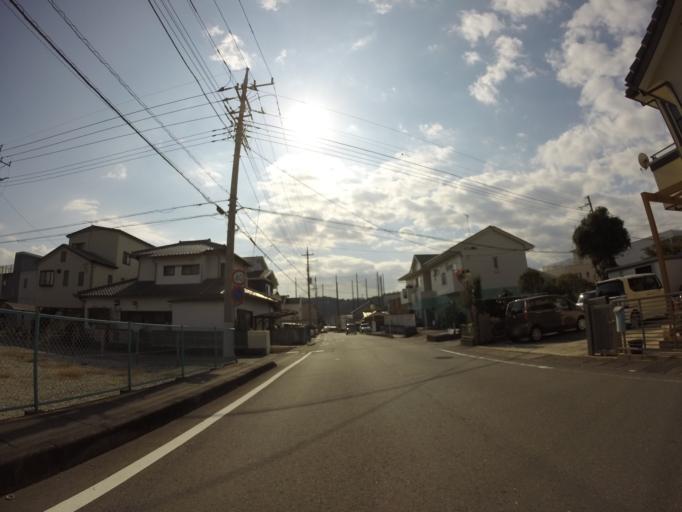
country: JP
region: Shizuoka
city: Fujinomiya
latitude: 35.2088
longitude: 138.6342
